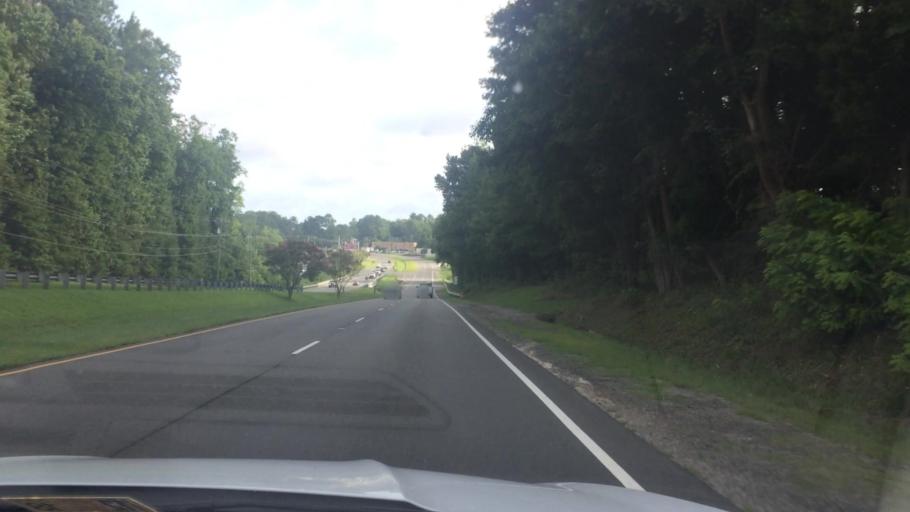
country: US
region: Virginia
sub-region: Gloucester County
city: Gloucester Courthouse
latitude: 37.4060
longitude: -76.5188
